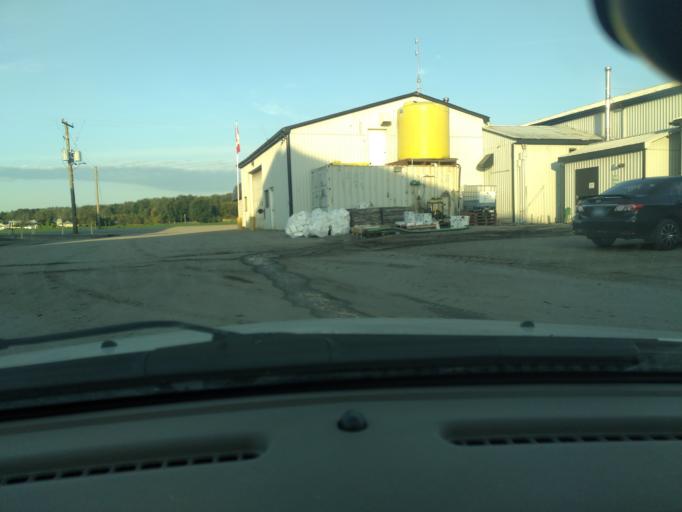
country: CA
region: Ontario
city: Bradford West Gwillimbury
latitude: 44.0407
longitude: -79.6227
